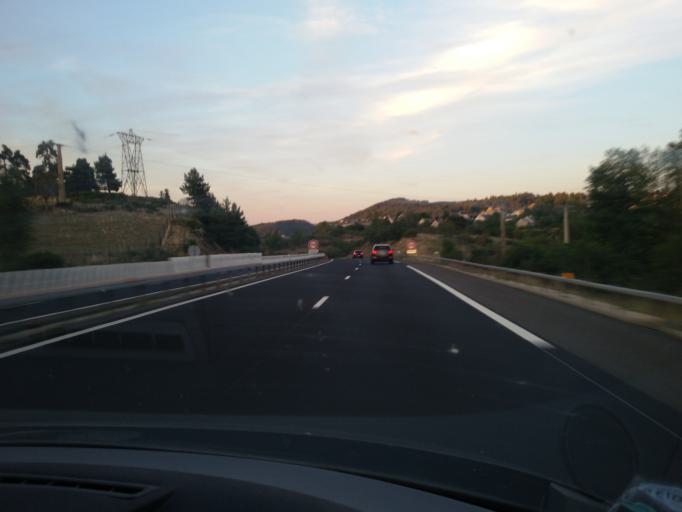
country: FR
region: Languedoc-Roussillon
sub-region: Departement de la Lozere
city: Aumont-Aubrac
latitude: 44.7212
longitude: 3.2757
